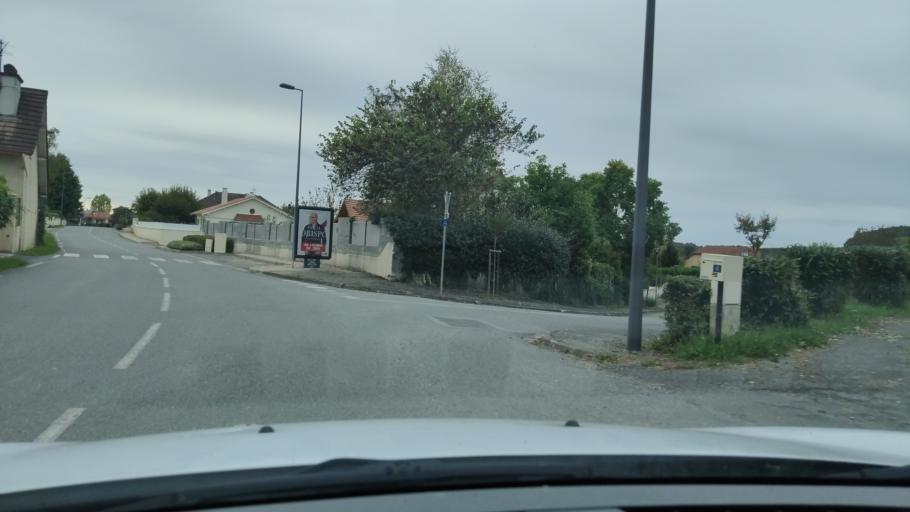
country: FR
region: Aquitaine
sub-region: Departement des Pyrenees-Atlantiques
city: Sauvagnon
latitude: 43.4053
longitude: -0.3800
